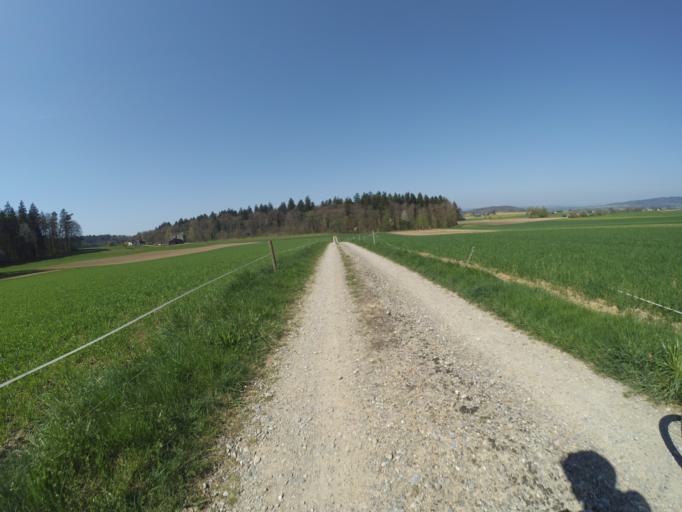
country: CH
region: Thurgau
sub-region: Frauenfeld District
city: Diessenhofen
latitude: 47.6544
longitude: 8.7508
